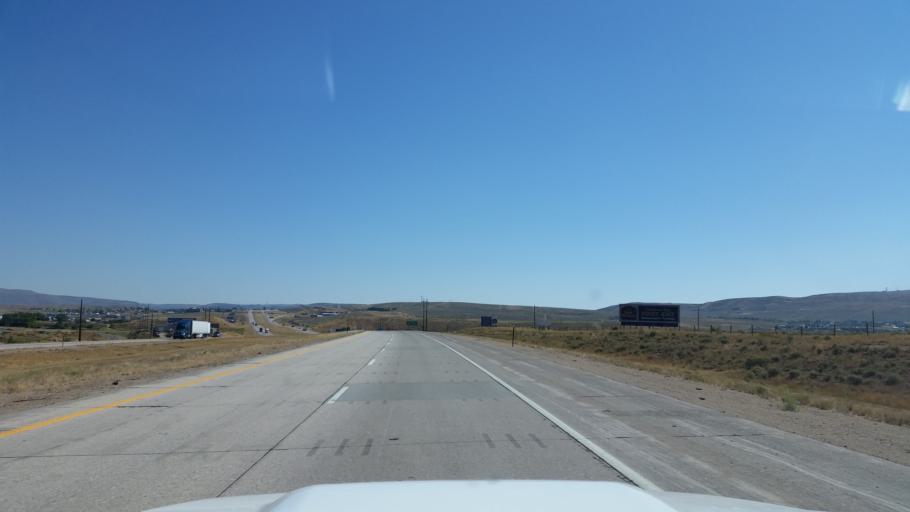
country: US
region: Wyoming
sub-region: Uinta County
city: Evanston
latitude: 41.2477
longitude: -111.0148
